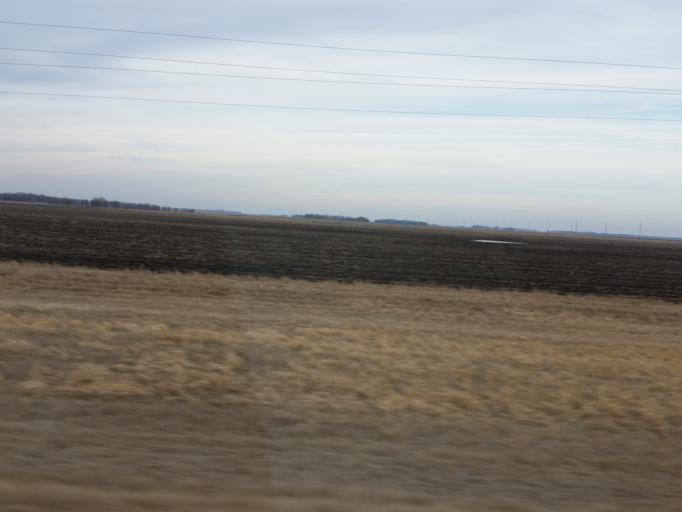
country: US
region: North Dakota
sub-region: Cass County
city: Casselton
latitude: 47.0689
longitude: -97.2180
